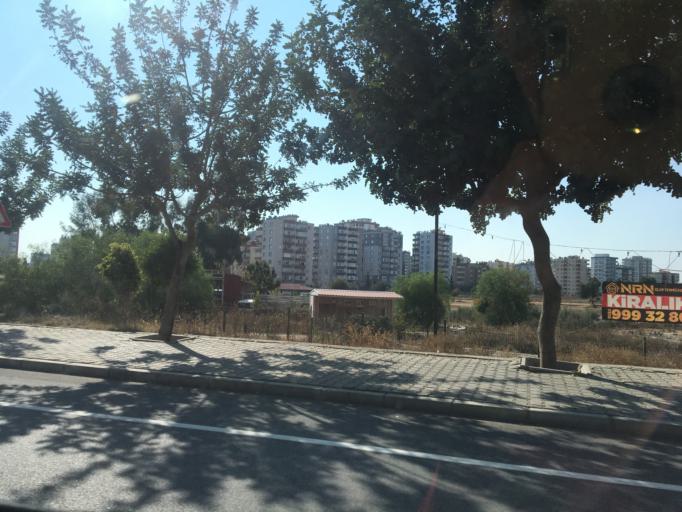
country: TR
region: Adana
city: Seyhan
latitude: 37.0367
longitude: 35.2801
